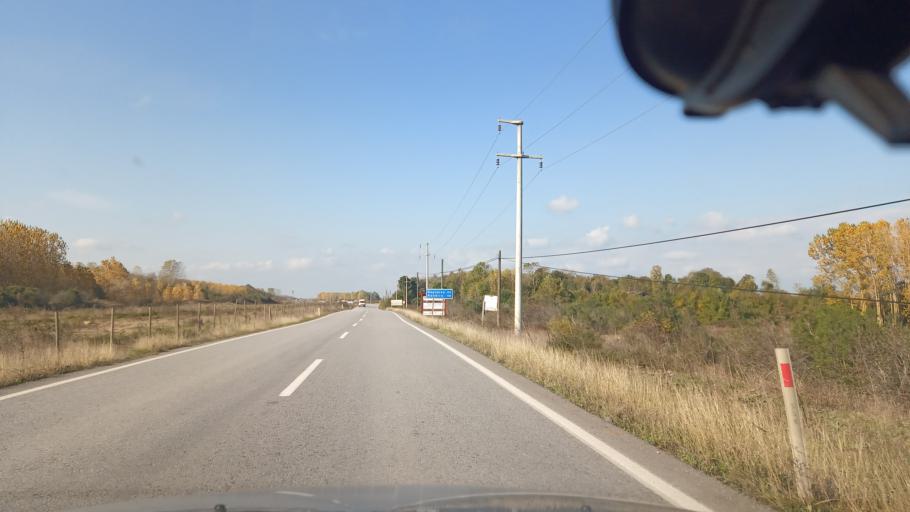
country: TR
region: Sakarya
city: Karasu
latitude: 41.1195
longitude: 30.6034
